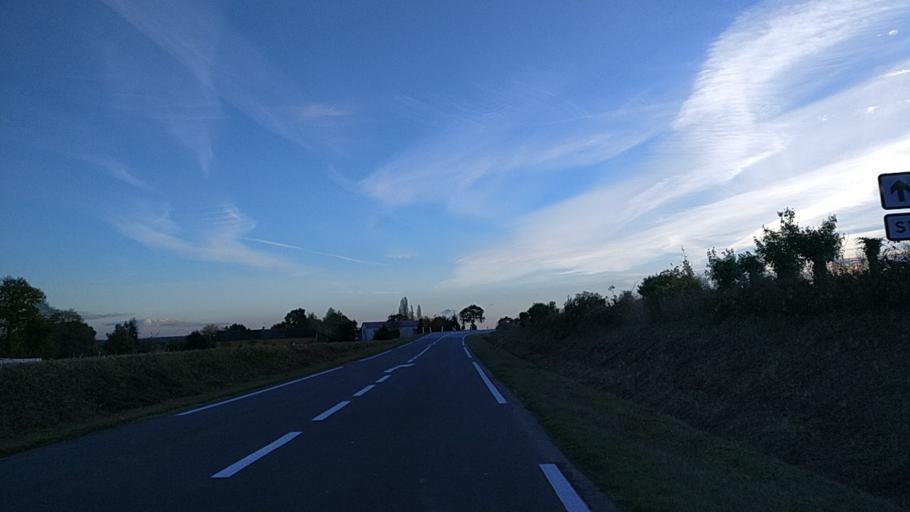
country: FR
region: Brittany
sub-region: Departement d'Ille-et-Vilaine
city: Chevaigne
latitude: 48.2114
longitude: -1.6218
